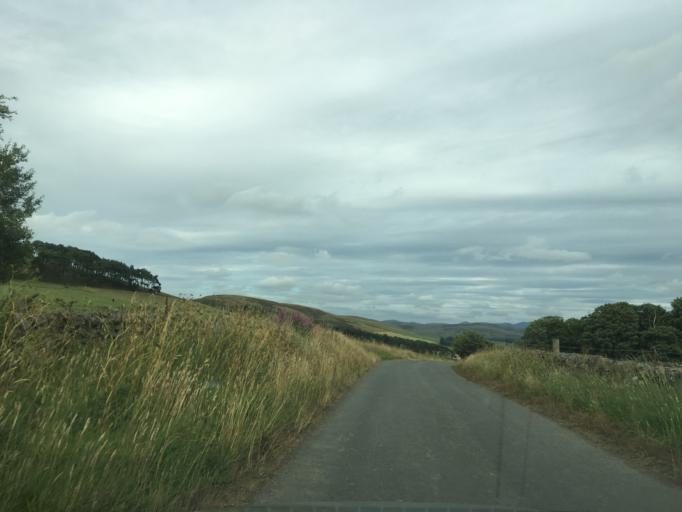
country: GB
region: Scotland
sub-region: South Lanarkshire
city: Douglas
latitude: 55.5115
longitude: -3.7327
